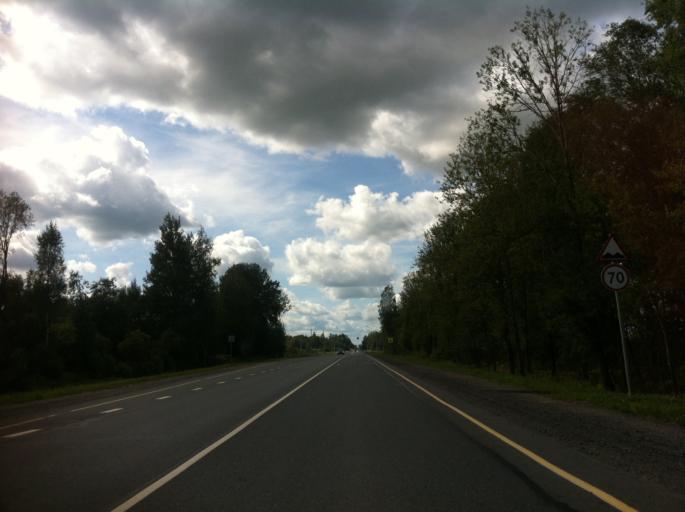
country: RU
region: Pskov
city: Pskov
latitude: 57.7731
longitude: 28.1369
